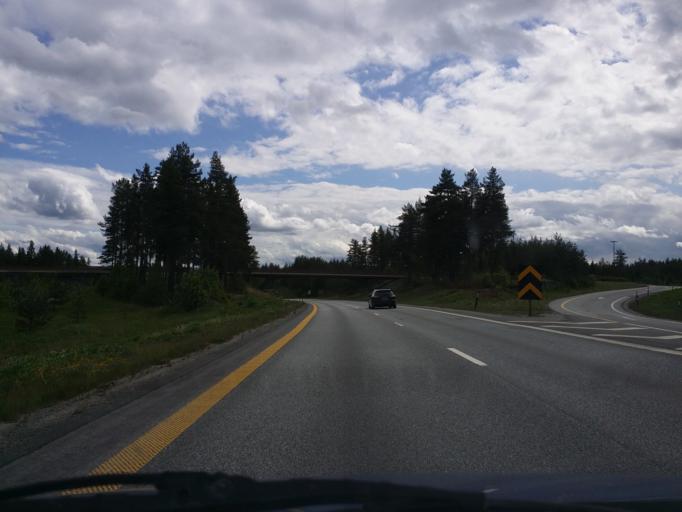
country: NO
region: Hedmark
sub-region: Stange
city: Stange
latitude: 60.6926
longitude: 11.2768
